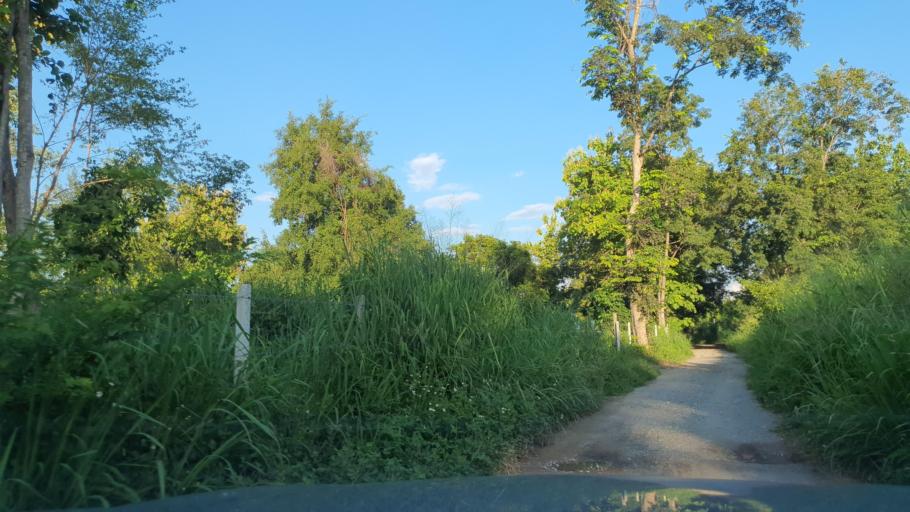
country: TH
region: Chiang Mai
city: Hang Dong
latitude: 18.6821
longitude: 98.8905
